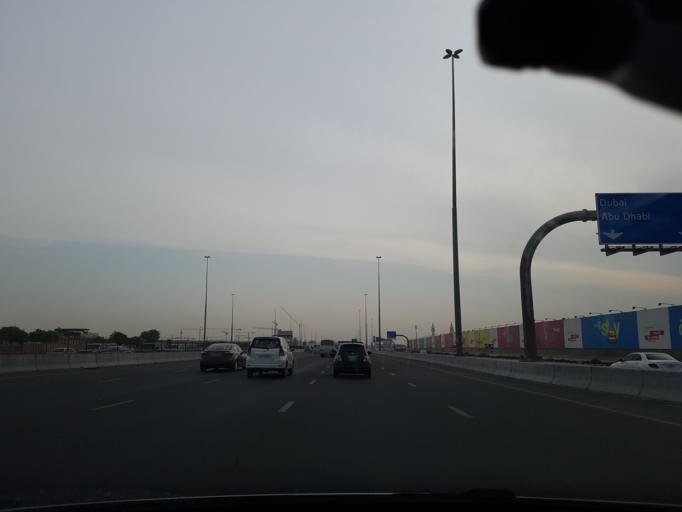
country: AE
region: Ash Shariqah
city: Sharjah
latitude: 25.3296
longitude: 55.4619
